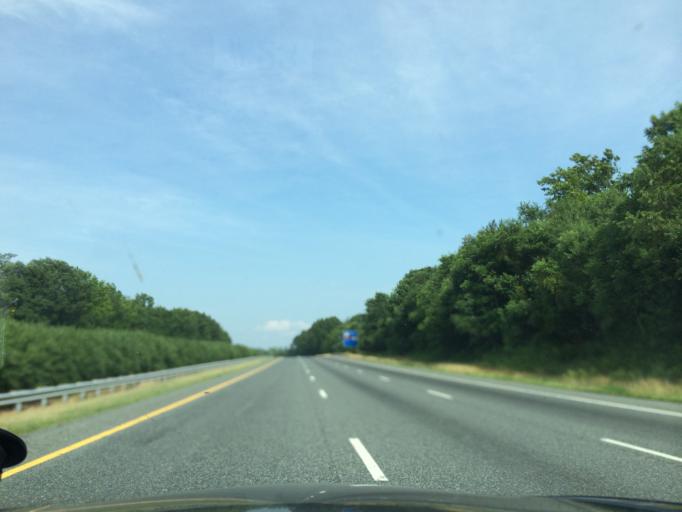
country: US
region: Maryland
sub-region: Carroll County
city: Mount Airy
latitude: 39.3499
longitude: -77.1082
